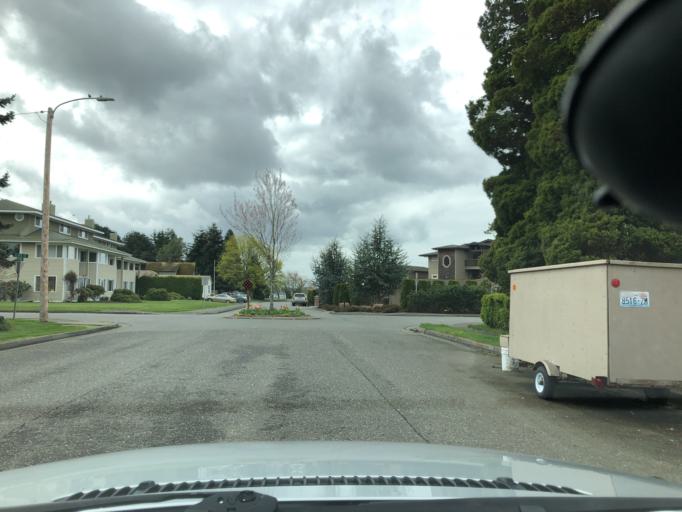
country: US
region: Washington
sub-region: Whatcom County
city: Blaine
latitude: 48.9879
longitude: -122.7481
